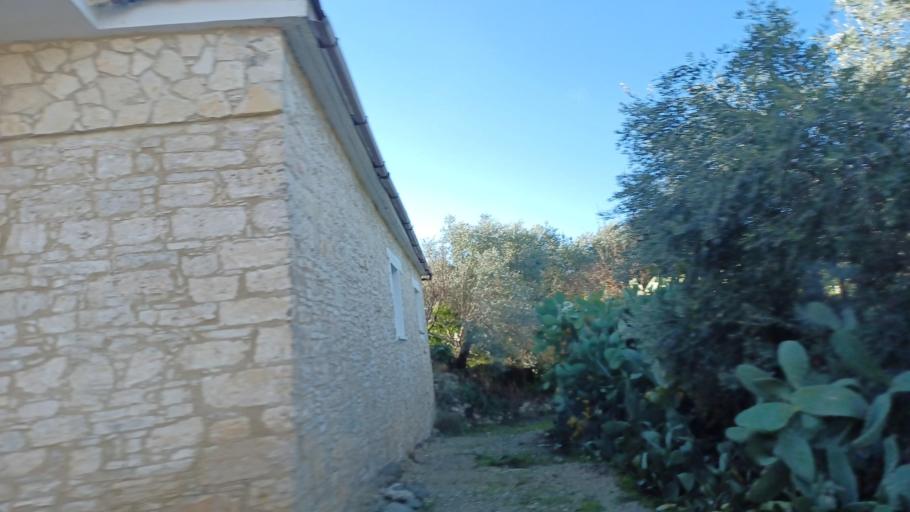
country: CY
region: Limassol
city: Pachna
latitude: 34.8521
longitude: 32.7426
